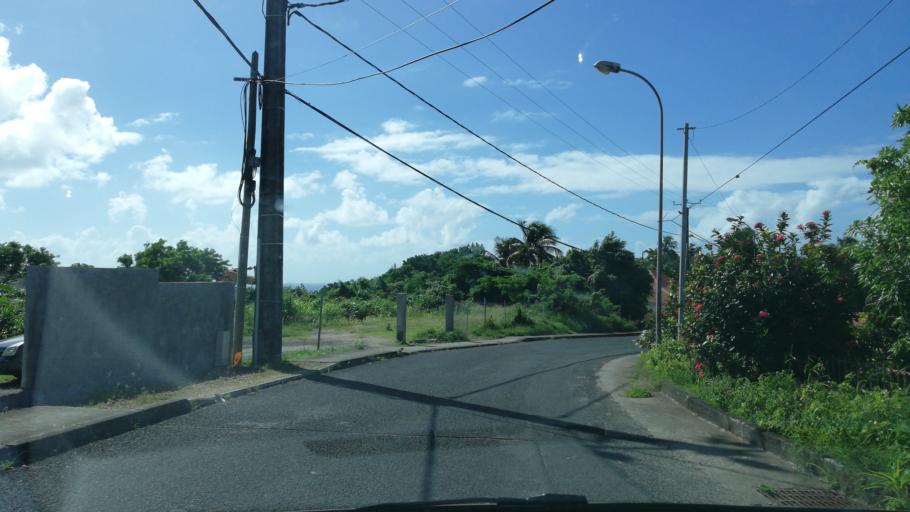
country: GP
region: Guadeloupe
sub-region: Guadeloupe
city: Le Gosier
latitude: 16.2138
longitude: -61.4547
